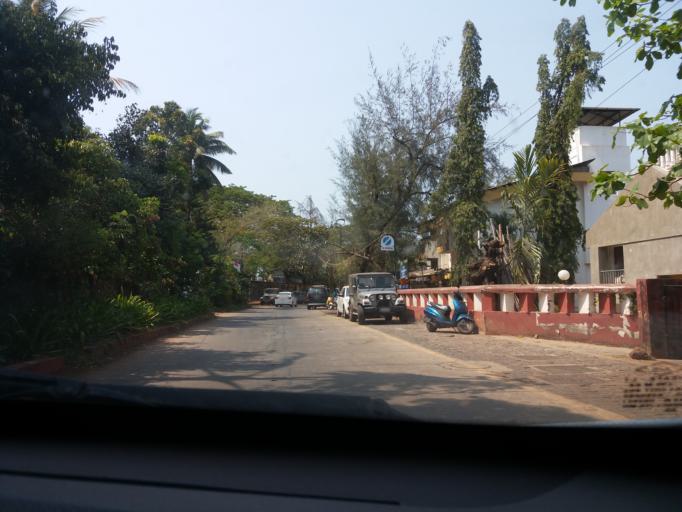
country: IN
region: Goa
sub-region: North Goa
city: Taleigao
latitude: 15.4556
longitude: 73.8031
